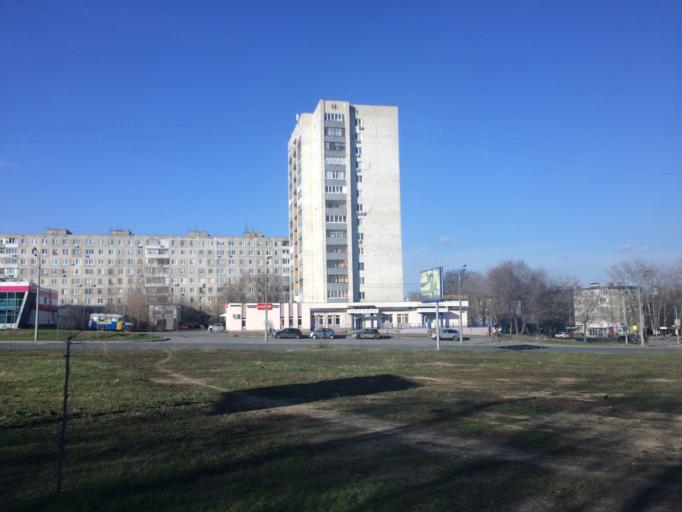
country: RU
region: Tatarstan
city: Staroye Arakchino
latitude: 55.8219
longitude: 49.0484
